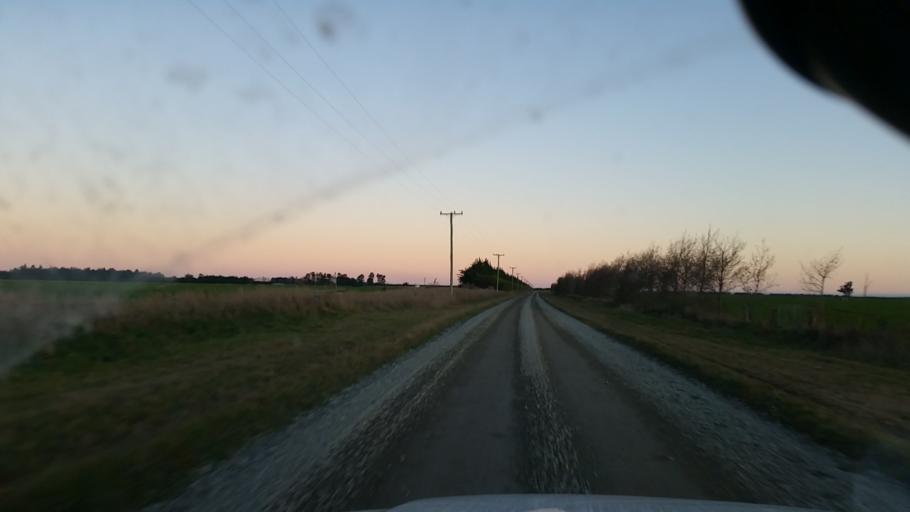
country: NZ
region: Canterbury
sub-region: Ashburton District
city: Tinwald
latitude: -44.0772
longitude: 171.6638
